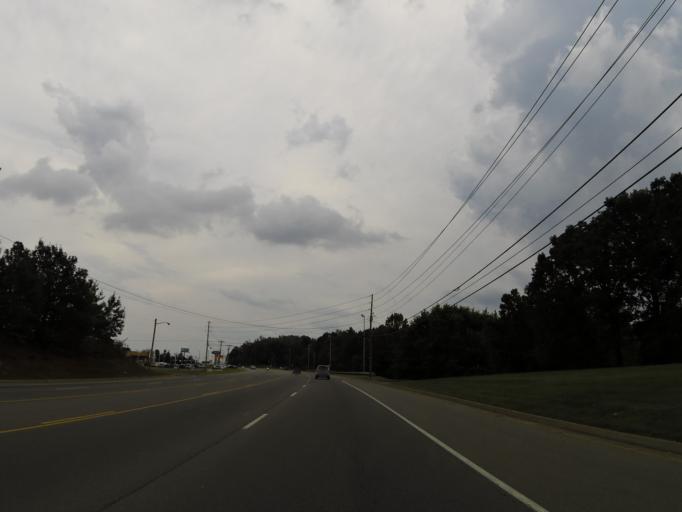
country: US
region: Tennessee
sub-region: Dickson County
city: Burns
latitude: 36.0376
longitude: -87.3570
